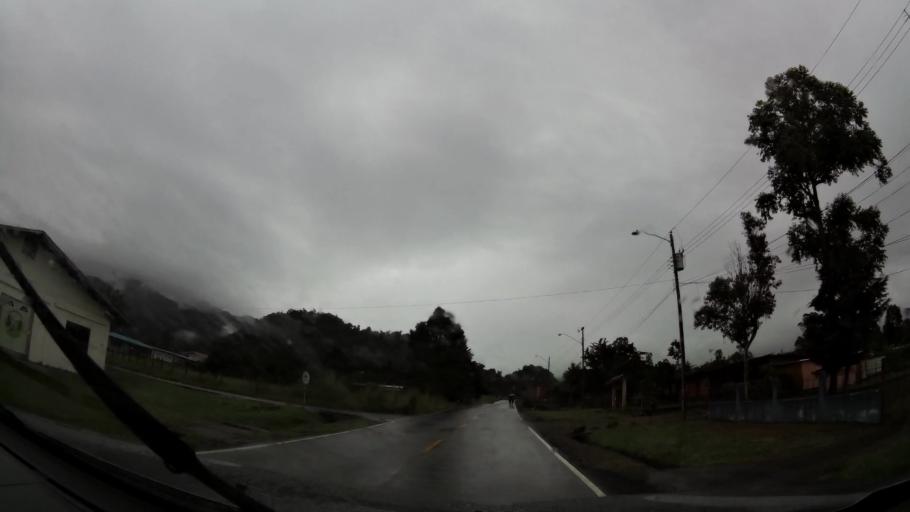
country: PA
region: Chiriqui
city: Volcan
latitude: 8.7944
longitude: -82.6478
